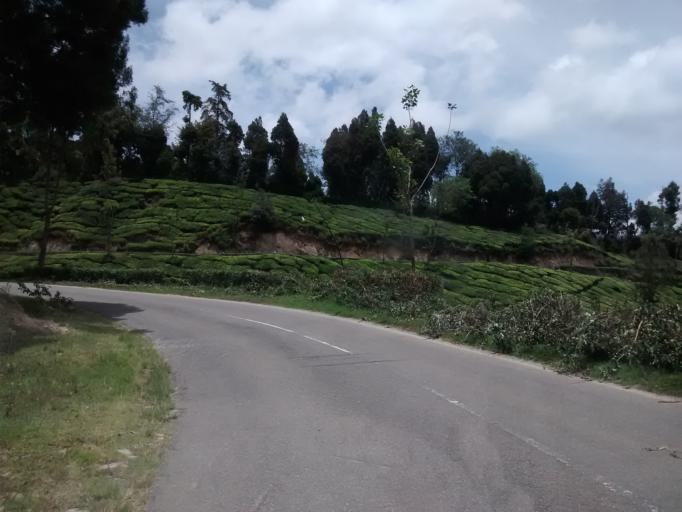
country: IN
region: Kerala
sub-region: Idukki
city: Munnar
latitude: 10.1289
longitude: 77.2227
